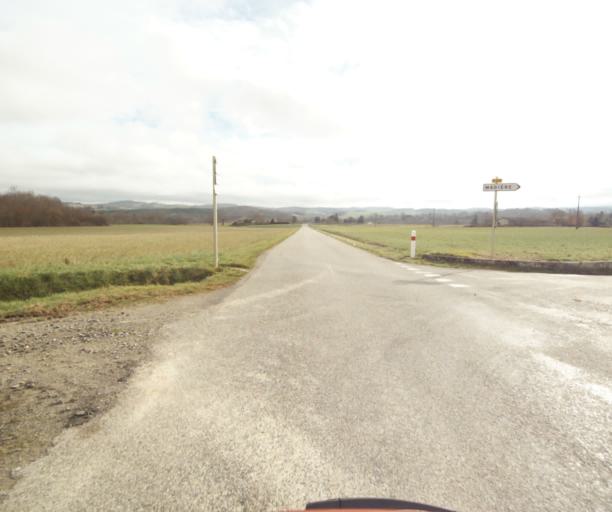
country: FR
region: Midi-Pyrenees
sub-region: Departement de l'Ariege
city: Pamiers
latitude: 43.1085
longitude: 1.5345
